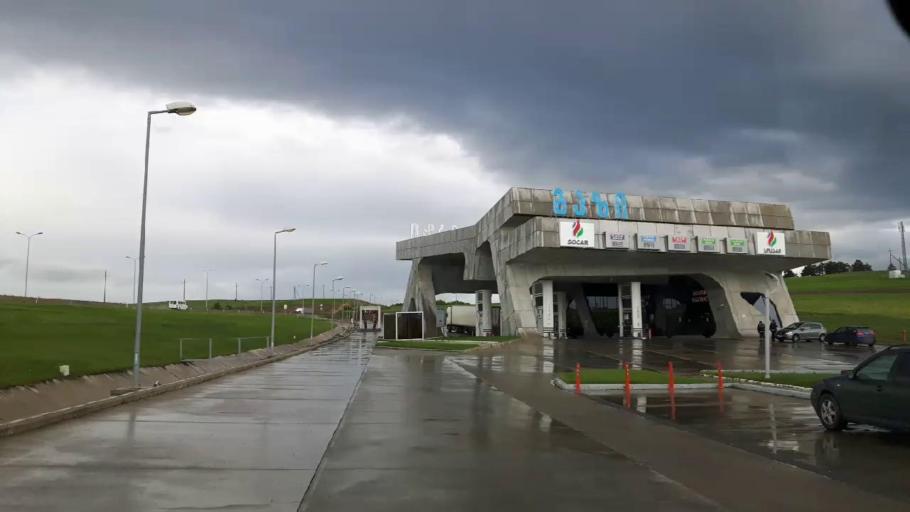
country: GE
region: Shida Kartli
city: Gori
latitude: 42.0160
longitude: 44.0289
